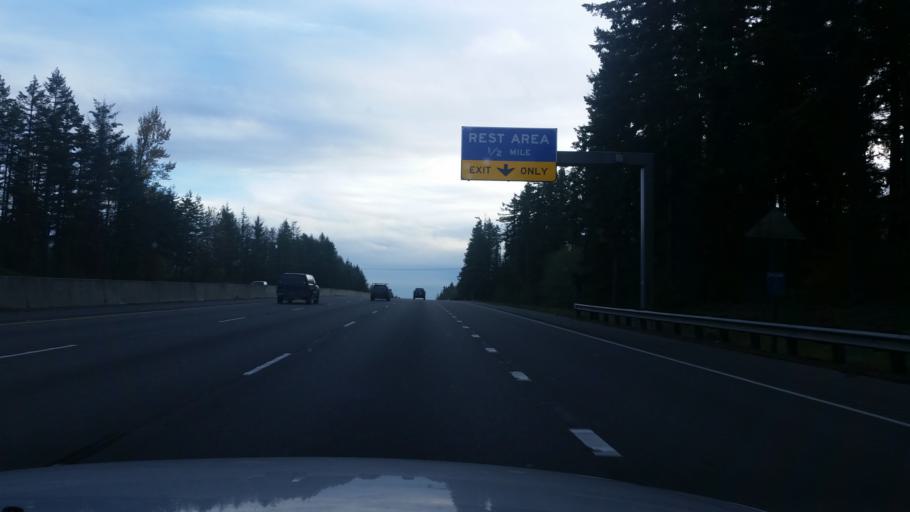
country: US
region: Washington
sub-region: Thurston County
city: Grand Mound
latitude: 46.8821
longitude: -122.9657
